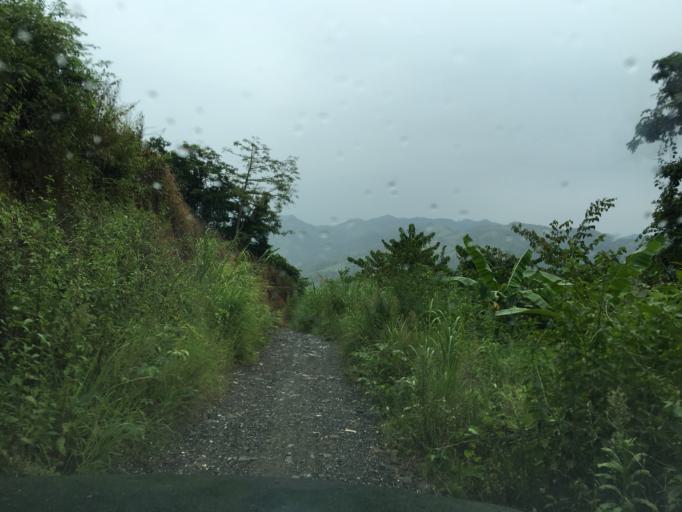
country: CN
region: Guangxi Zhuangzu Zizhiqu
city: Tongle
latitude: 25.0050
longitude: 105.9908
